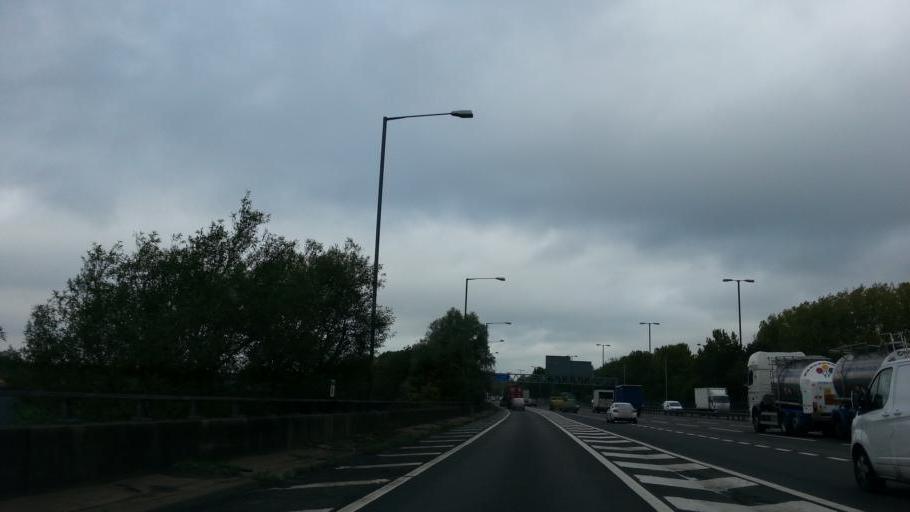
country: GB
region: England
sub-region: Walsall
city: Walsall
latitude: 52.5582
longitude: -1.9783
